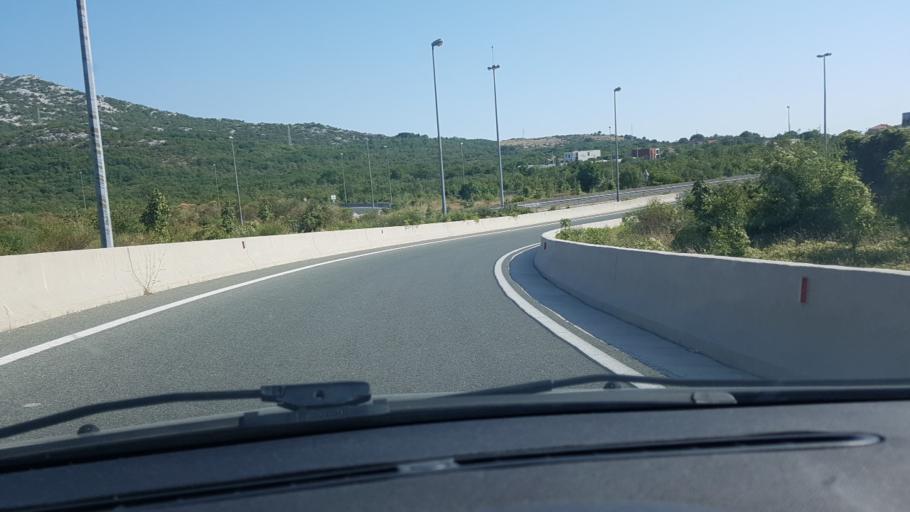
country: HR
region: Splitsko-Dalmatinska
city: Klis
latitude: 43.5757
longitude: 16.5379
